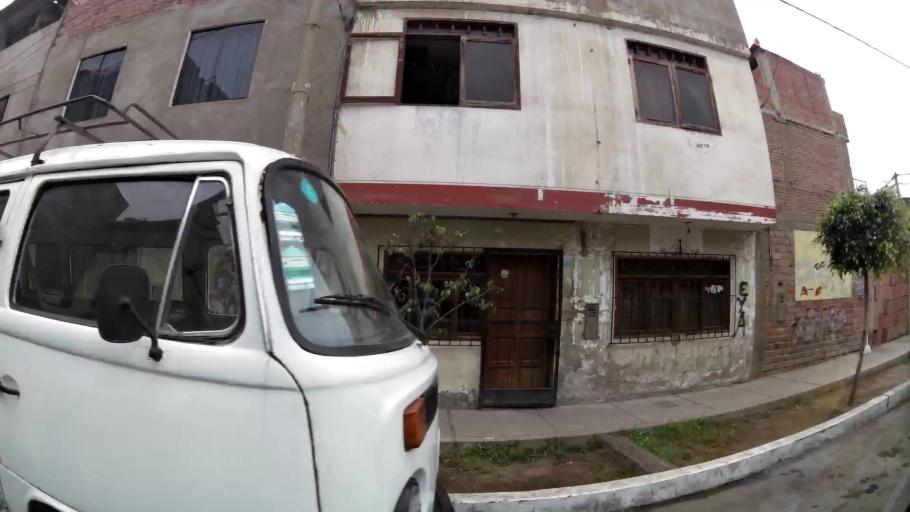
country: PE
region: Lima
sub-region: Lima
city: Surco
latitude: -12.1148
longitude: -77.0136
